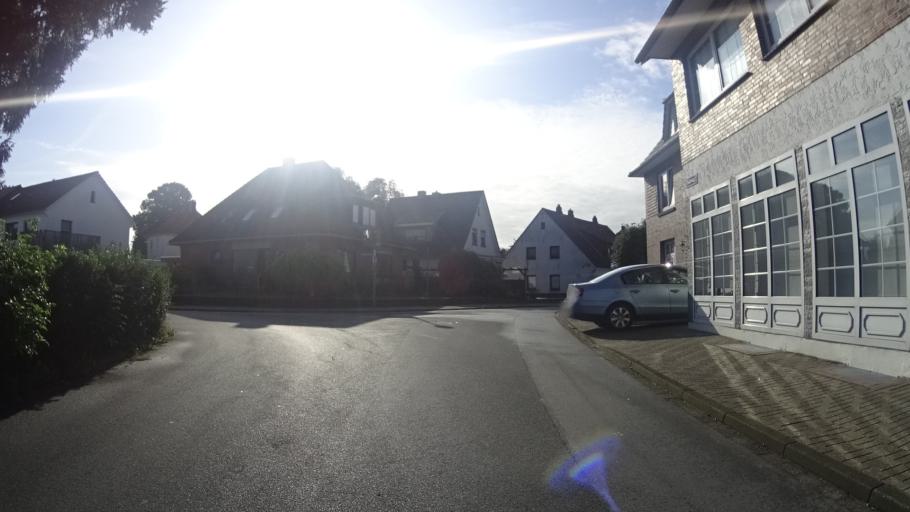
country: DE
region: Lower Saxony
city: Nordenham
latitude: 53.4944
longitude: 8.4688
